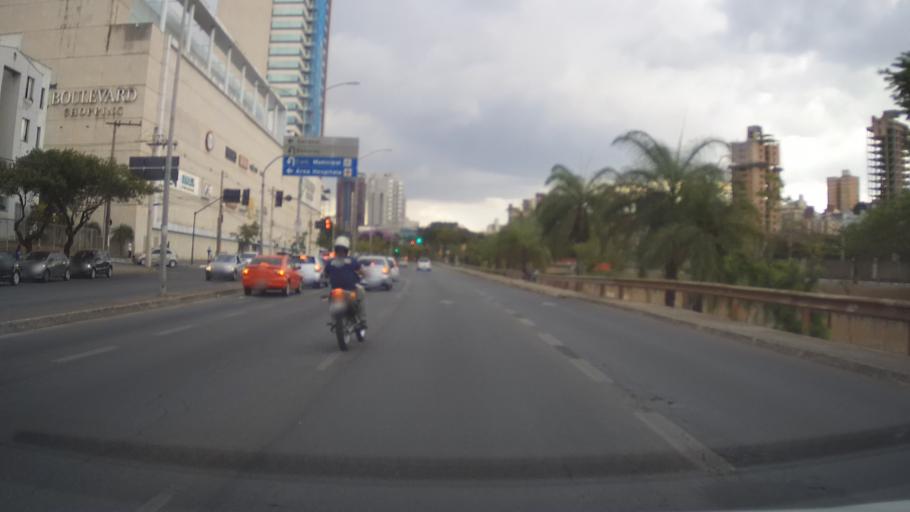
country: BR
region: Minas Gerais
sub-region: Belo Horizonte
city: Belo Horizonte
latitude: -19.9196
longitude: -43.9189
